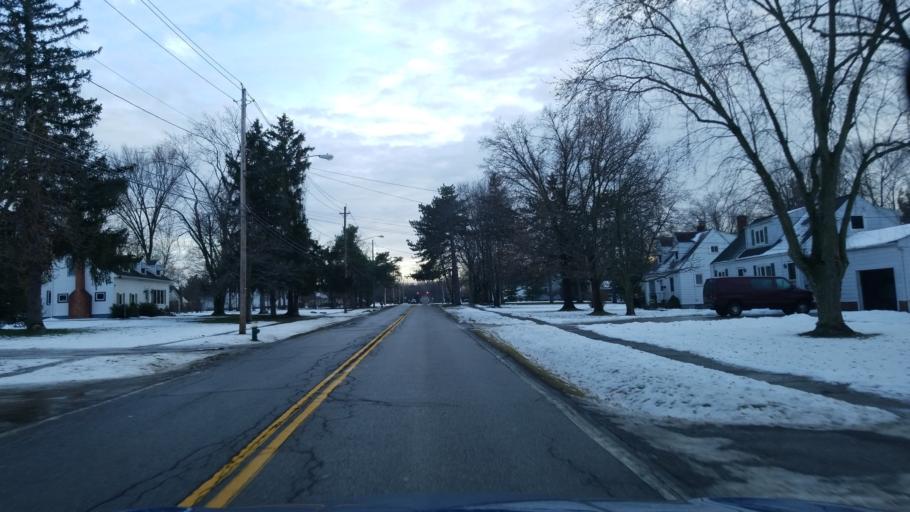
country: US
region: Ohio
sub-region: Cuyahoga County
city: Strongsville
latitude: 41.3116
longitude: -81.8277
